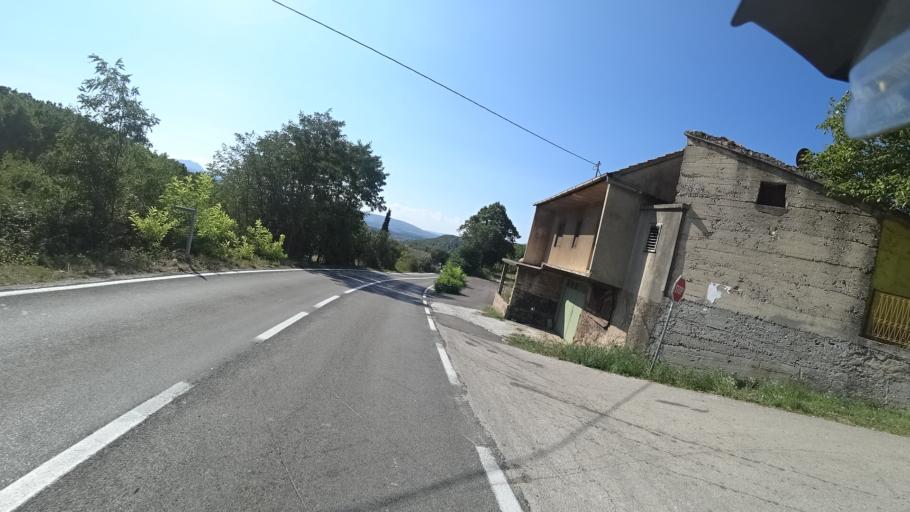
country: HR
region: Sibensko-Kniniska
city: Knin
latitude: 44.0145
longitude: 16.1971
